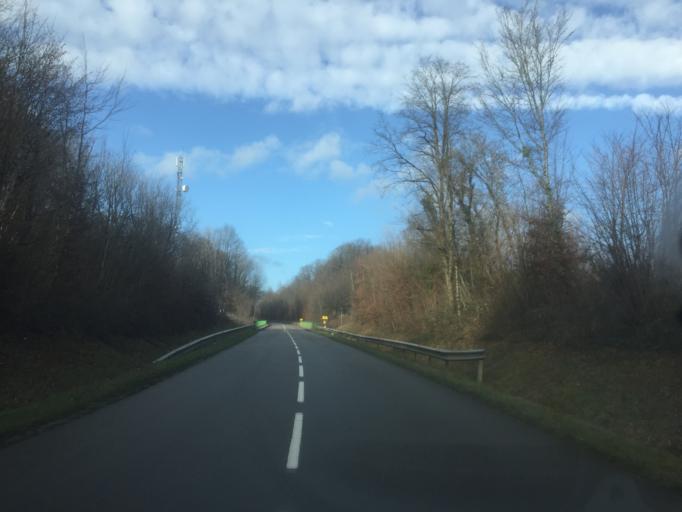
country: FR
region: Franche-Comte
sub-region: Departement du Doubs
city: Saint-Vit
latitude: 47.1969
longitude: 5.8074
